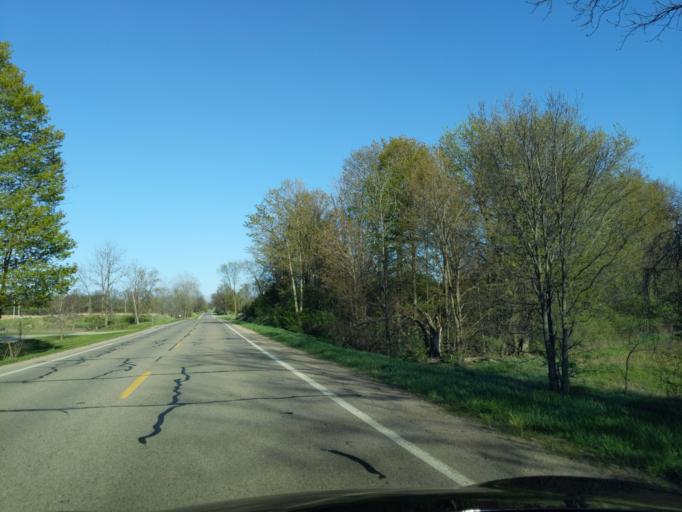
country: US
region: Michigan
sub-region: Eaton County
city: Grand Ledge
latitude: 42.8118
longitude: -84.8087
